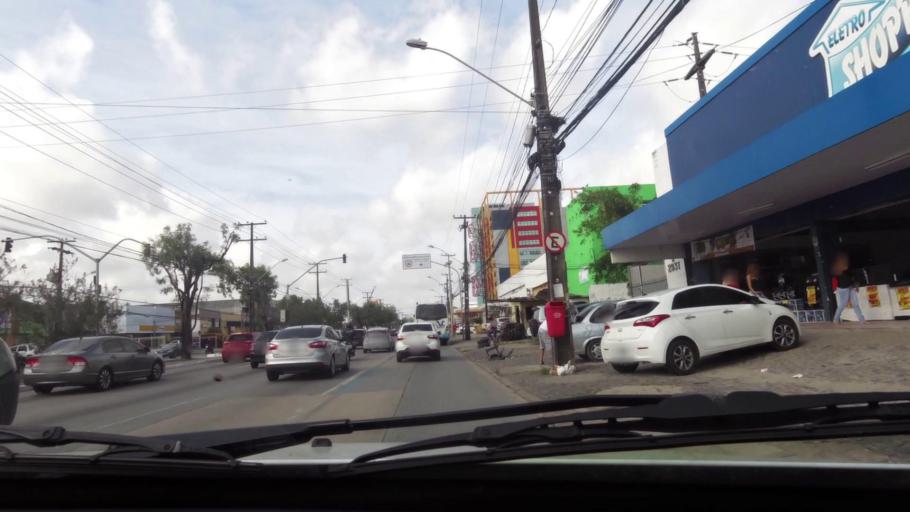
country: BR
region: Pernambuco
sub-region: Recife
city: Recife
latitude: -8.1028
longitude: -34.9106
